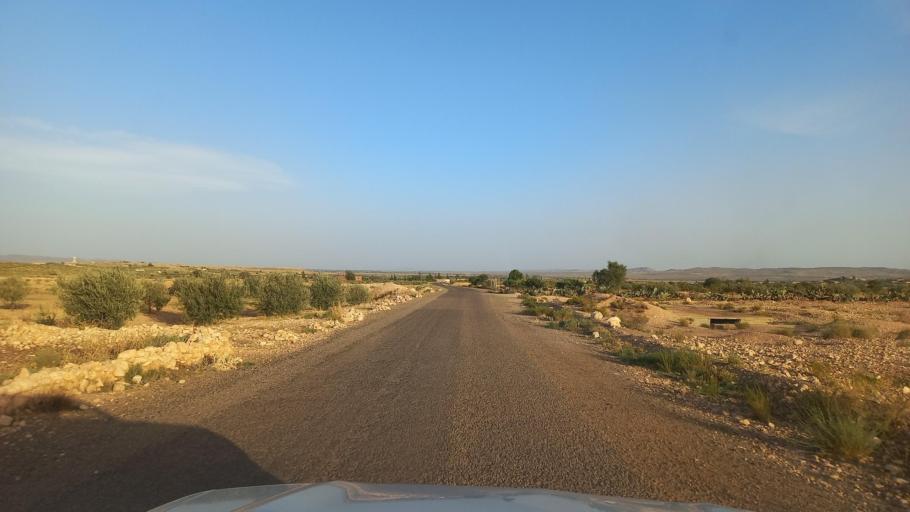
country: TN
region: Al Qasrayn
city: Kasserine
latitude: 35.2732
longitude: 8.9239
